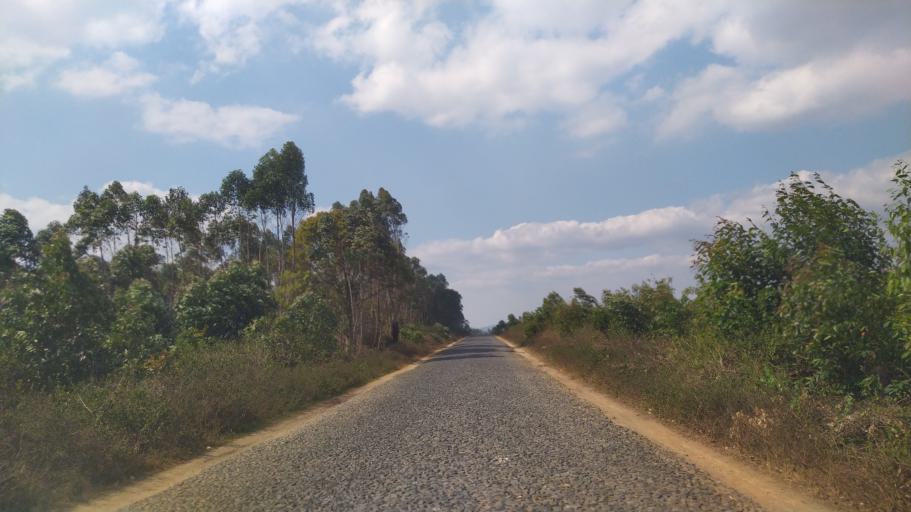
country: MG
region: Alaotra Mangoro
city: Moramanga
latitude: -18.7753
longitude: 48.2498
